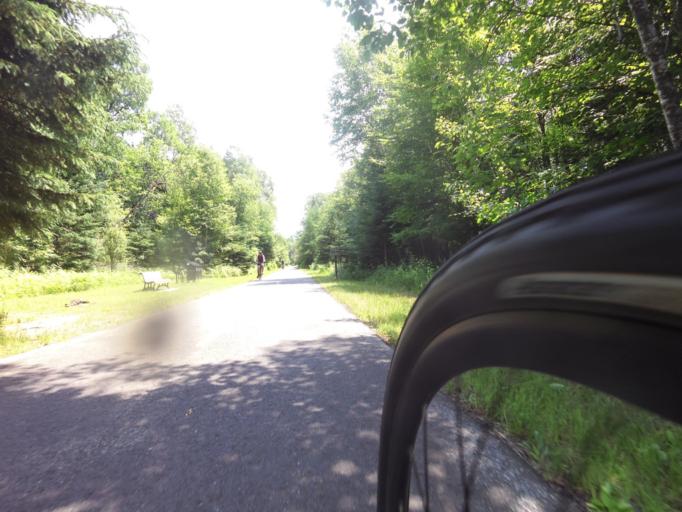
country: CA
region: Quebec
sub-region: Laurentides
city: Mont-Tremblant
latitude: 46.1543
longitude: -74.5980
